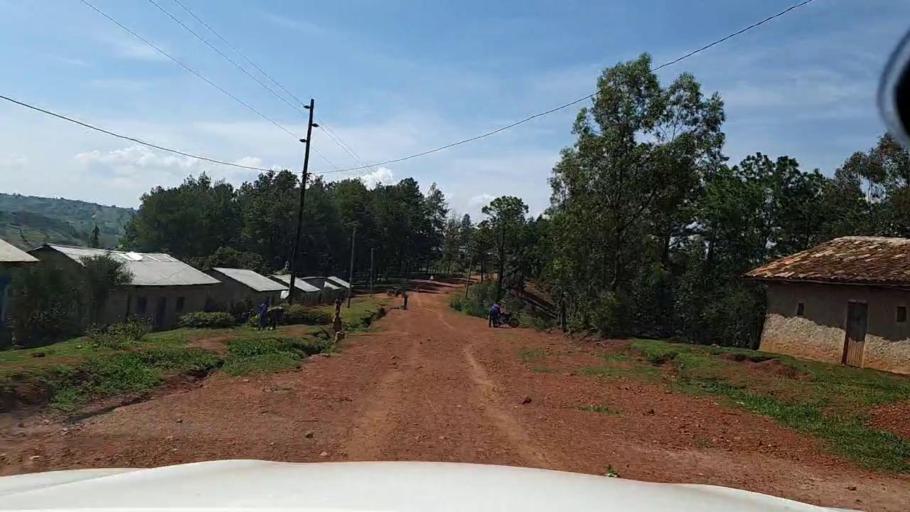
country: RW
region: Southern Province
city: Butare
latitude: -2.7152
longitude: 29.8395
